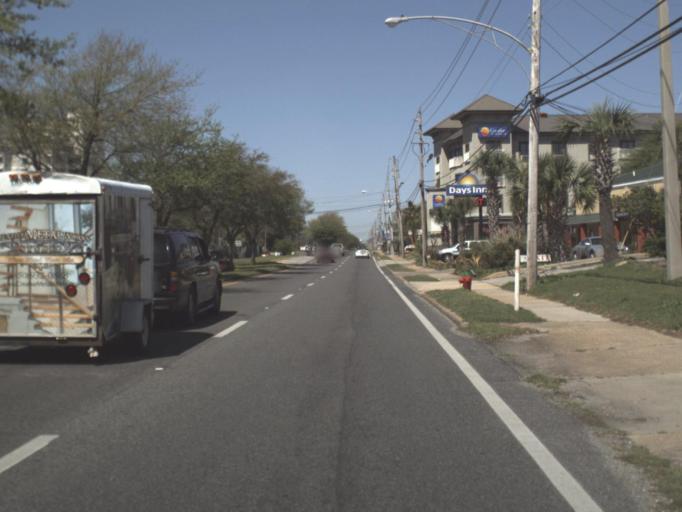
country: US
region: Florida
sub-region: Okaloosa County
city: Fort Walton Beach
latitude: 30.4052
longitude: -86.6229
